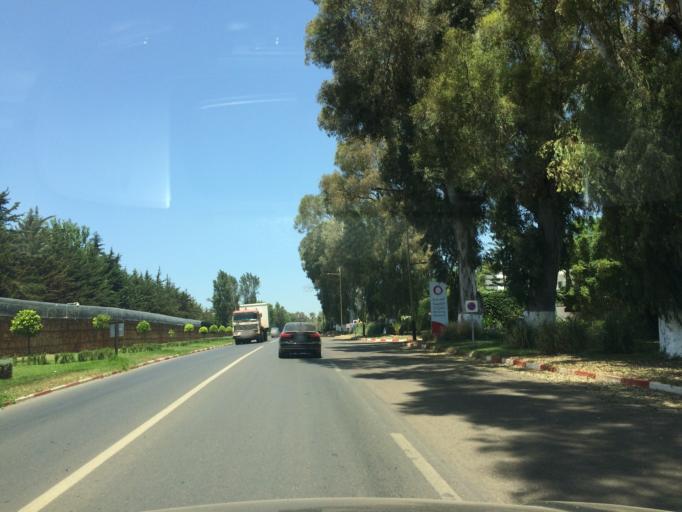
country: MA
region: Rabat-Sale-Zemmour-Zaer
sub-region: Skhirate-Temara
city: Temara
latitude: 33.9222
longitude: -6.8207
